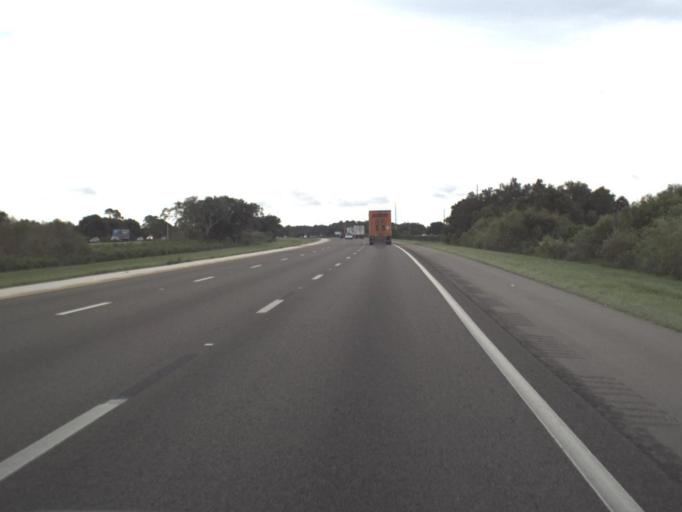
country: US
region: Florida
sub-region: Sarasota County
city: Laurel
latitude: 27.1759
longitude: -82.4354
